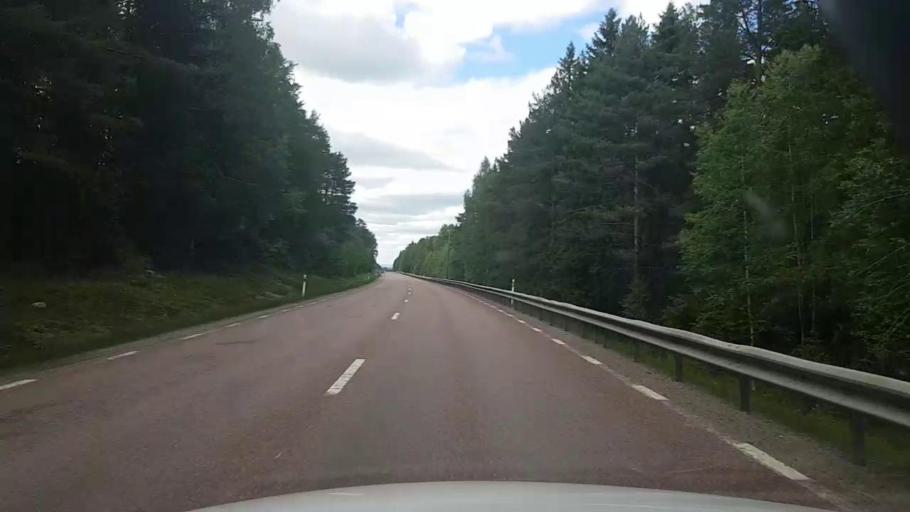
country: SE
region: Gaevleborg
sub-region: Ljusdals Kommun
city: Ljusdal
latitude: 61.7949
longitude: 16.1265
